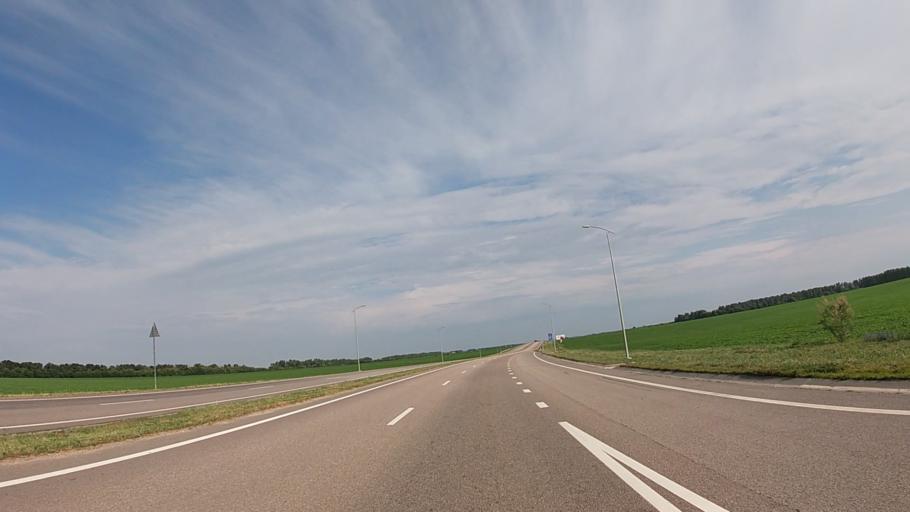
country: RU
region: Belgorod
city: Rakitnoye
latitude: 50.7926
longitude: 35.8653
